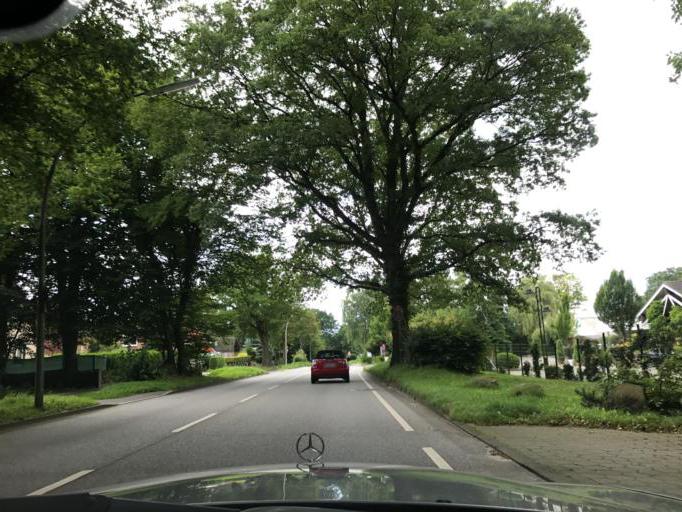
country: DE
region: Schleswig-Holstein
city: Oststeinbek
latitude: 53.5128
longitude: 10.1762
